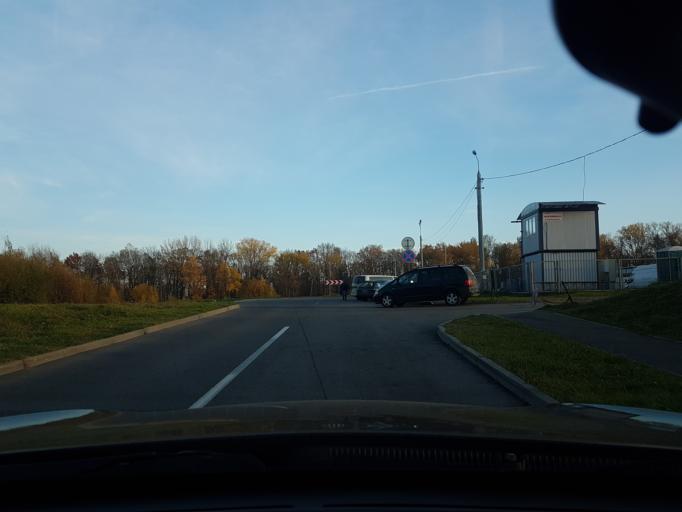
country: BY
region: Minsk
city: Yubilyeyny
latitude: 53.8476
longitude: 27.4900
